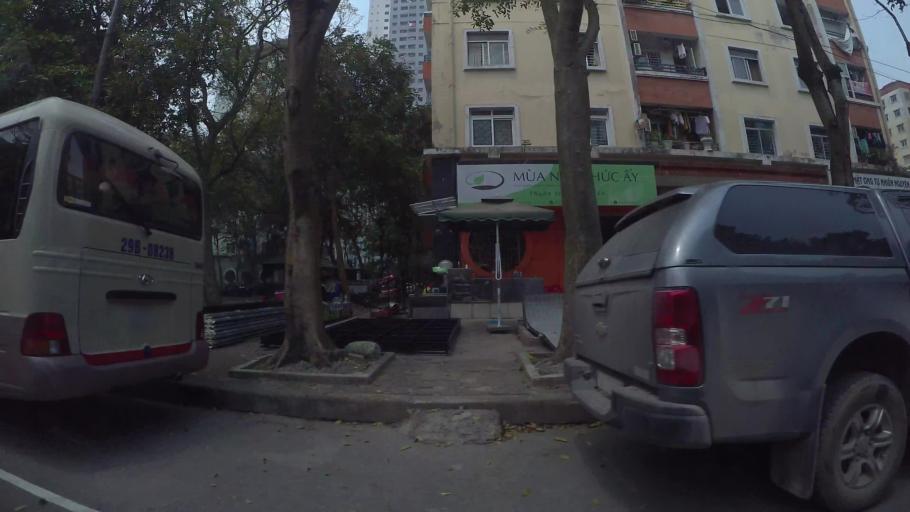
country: VN
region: Ha Noi
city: Van Dien
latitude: 20.9636
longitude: 105.8329
